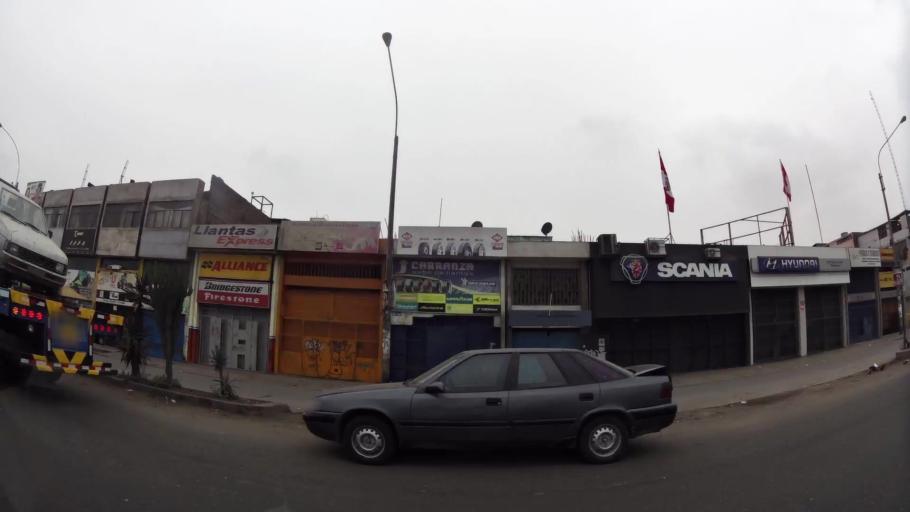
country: PE
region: Lima
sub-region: Lima
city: San Luis
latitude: -12.0749
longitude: -77.0096
